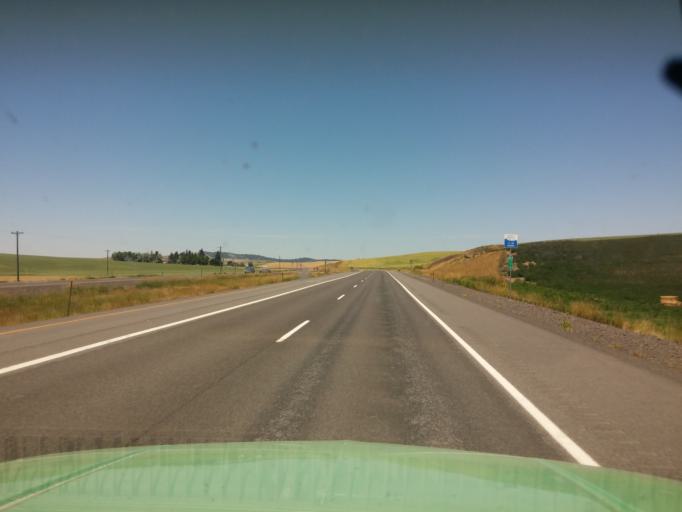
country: US
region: Idaho
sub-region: Latah County
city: Moscow
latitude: 46.5909
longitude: -116.9433
